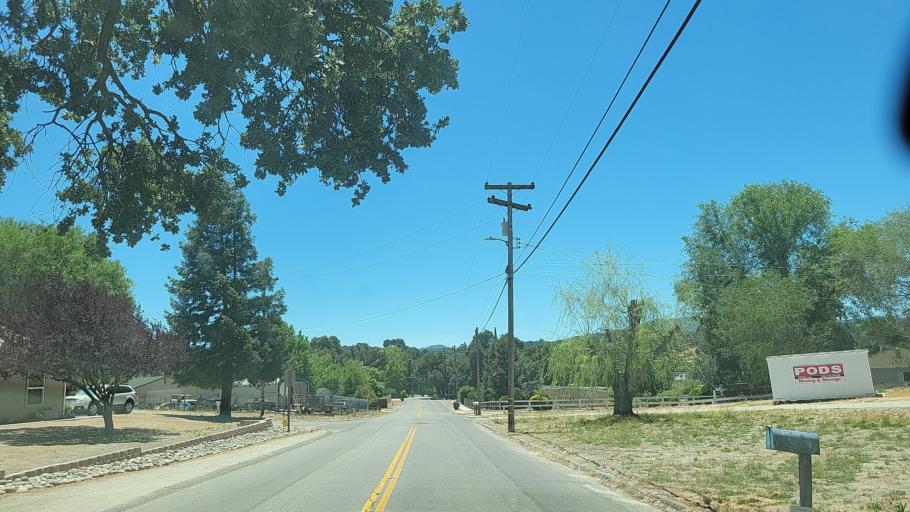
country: US
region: California
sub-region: San Luis Obispo County
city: Atascadero
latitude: 35.5025
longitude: -120.6829
